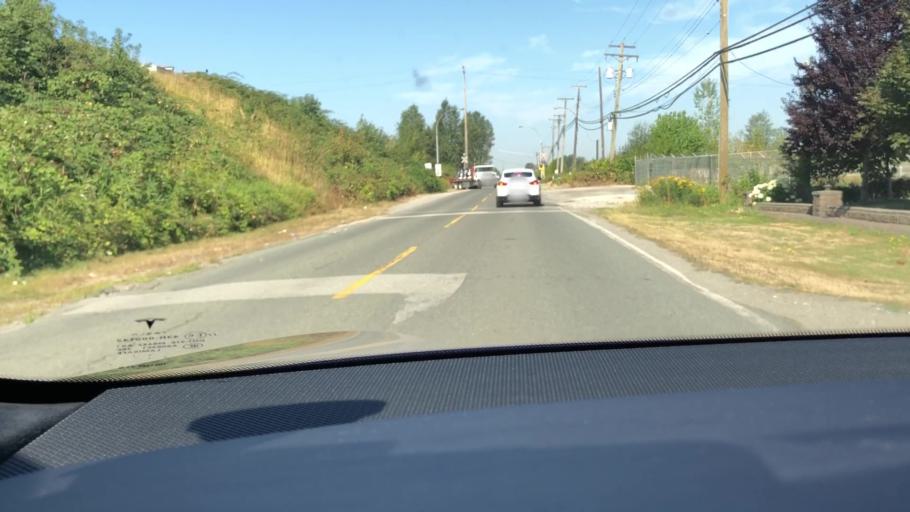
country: CA
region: British Columbia
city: New Westminster
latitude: 49.1698
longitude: -122.9971
